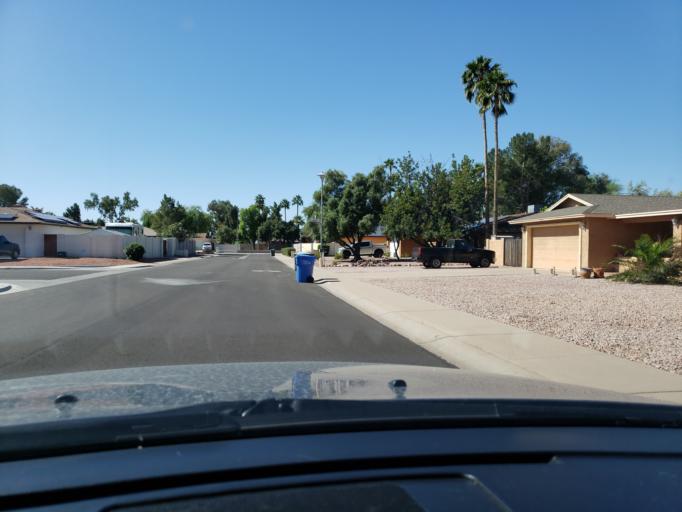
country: US
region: Arizona
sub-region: Maricopa County
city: Paradise Valley
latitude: 33.6135
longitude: -111.9552
